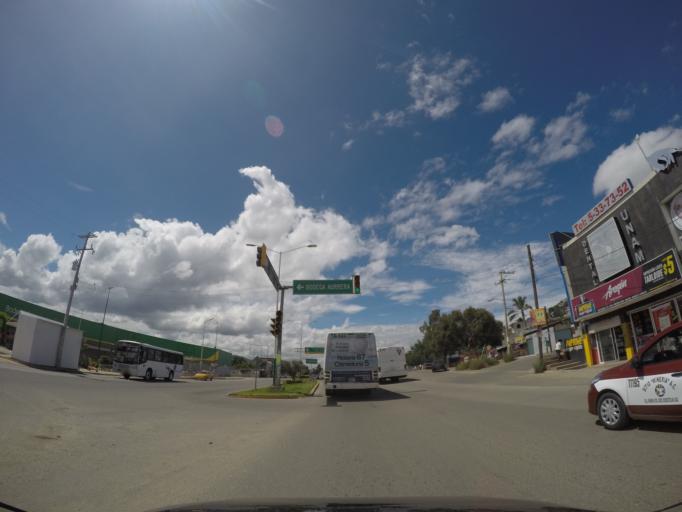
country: MX
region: Oaxaca
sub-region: Santa Cruz Xoxocotlan
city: Santa Cruz Xoxocotlan
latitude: 17.0456
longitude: -96.7310
